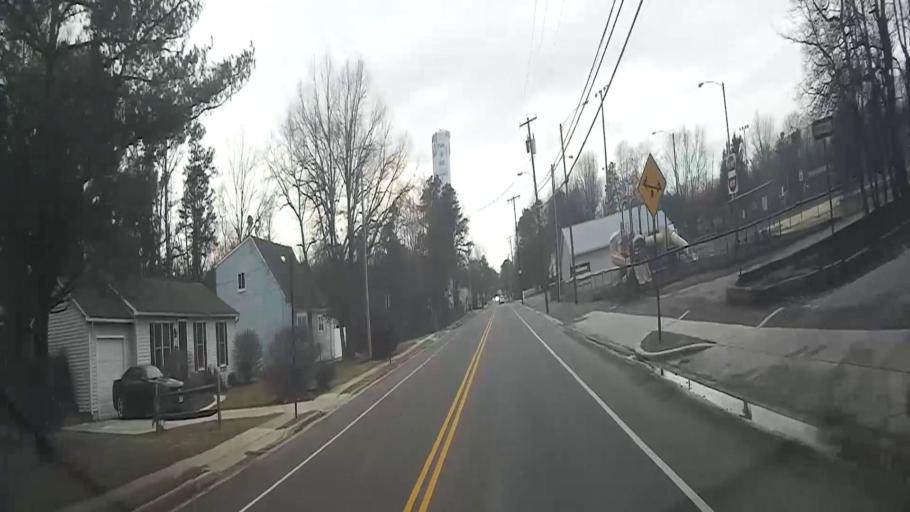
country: US
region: New Jersey
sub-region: Camden County
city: Pine Hill
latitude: 39.7780
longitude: -74.9818
